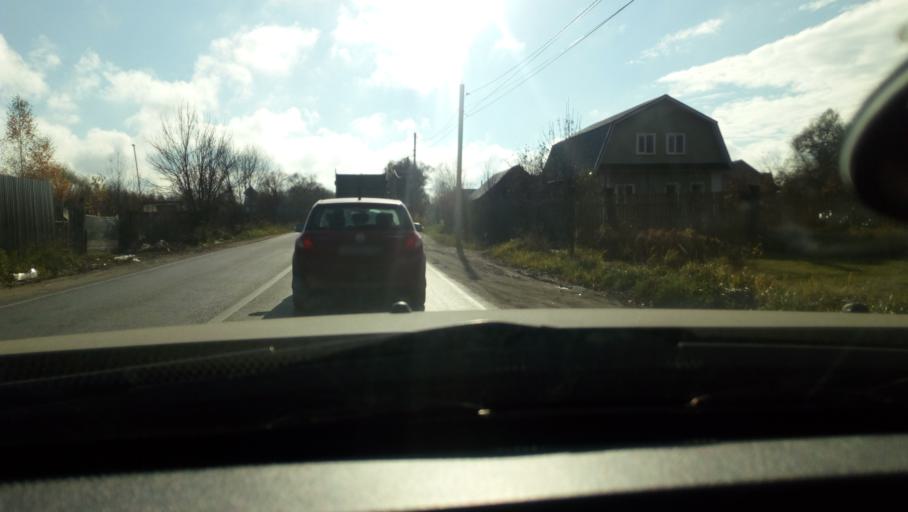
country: RU
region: Moskovskaya
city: Fryazevo
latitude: 55.7235
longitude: 38.4655
